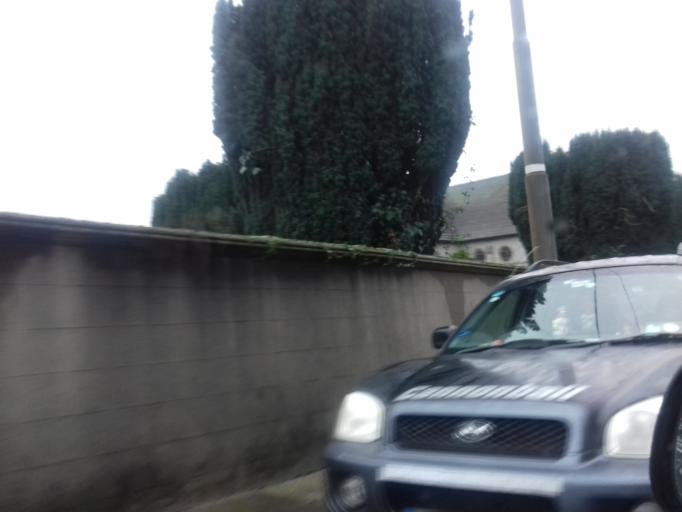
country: IE
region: Leinster
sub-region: Kilkenny
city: Graiguenamanagh
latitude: 52.5415
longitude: -6.9537
